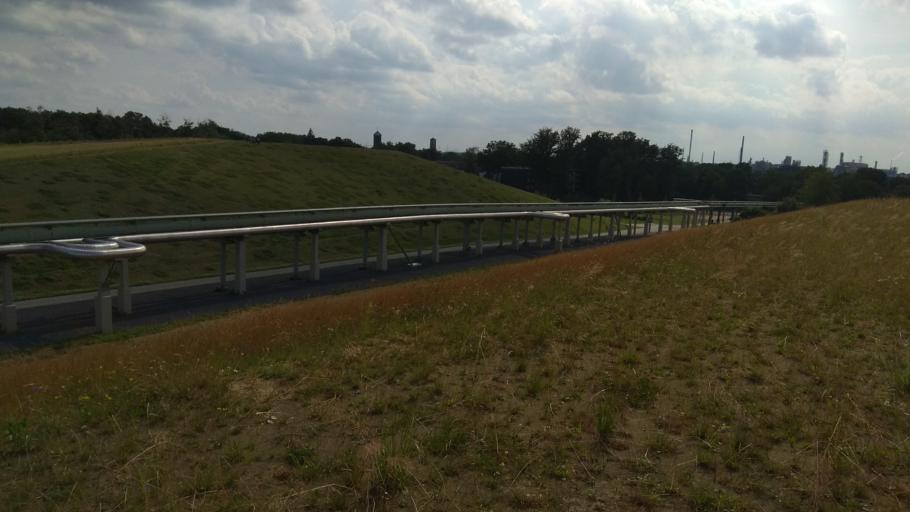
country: DE
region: North Rhine-Westphalia
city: Marl
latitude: 51.5992
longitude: 7.0575
